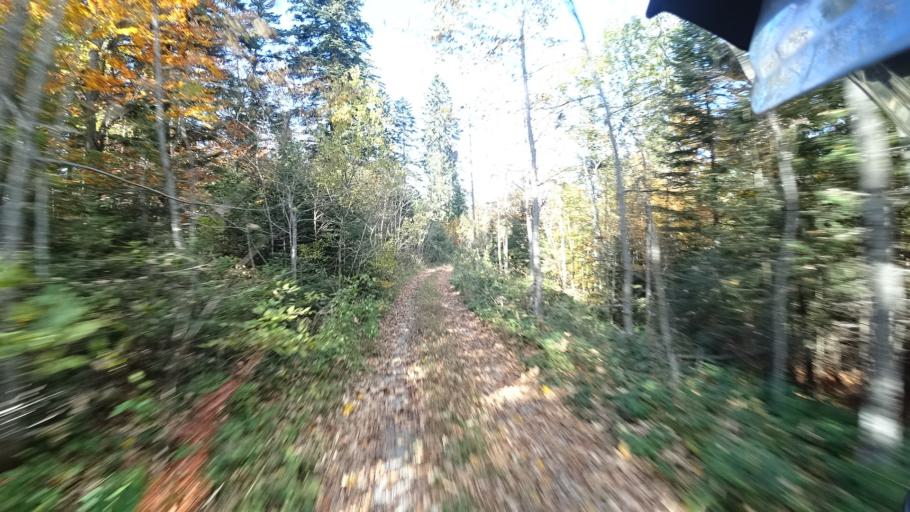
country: HR
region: Karlovacka
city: Plaski
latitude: 45.0557
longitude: 15.3308
